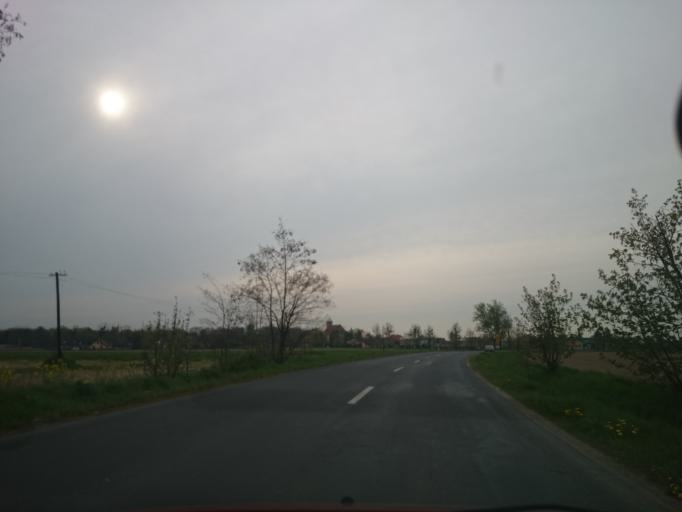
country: PL
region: Opole Voivodeship
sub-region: Powiat nyski
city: Sidzina
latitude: 50.6463
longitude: 17.4596
